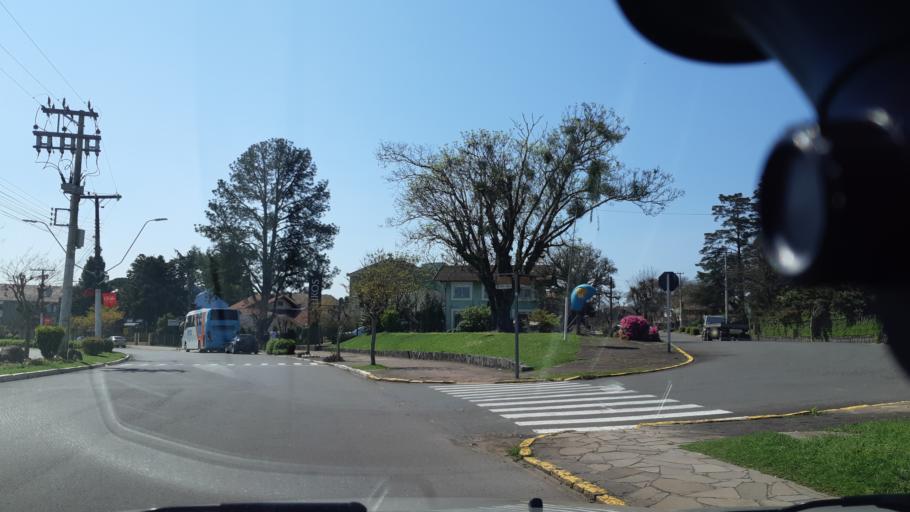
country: BR
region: Rio Grande do Sul
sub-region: Nova Petropolis
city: Nova Petropolis
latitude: -29.3826
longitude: -51.1166
